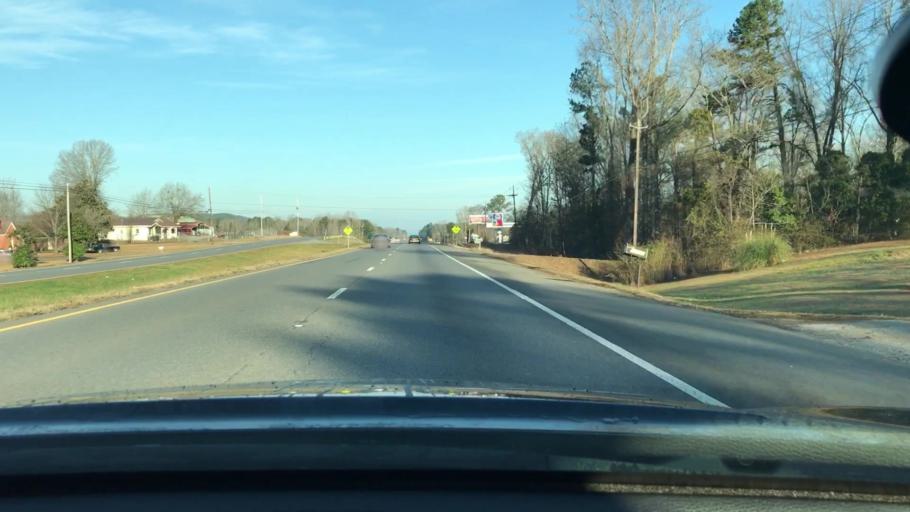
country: US
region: Alabama
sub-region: Talladega County
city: Childersburg
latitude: 33.2282
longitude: -86.3246
